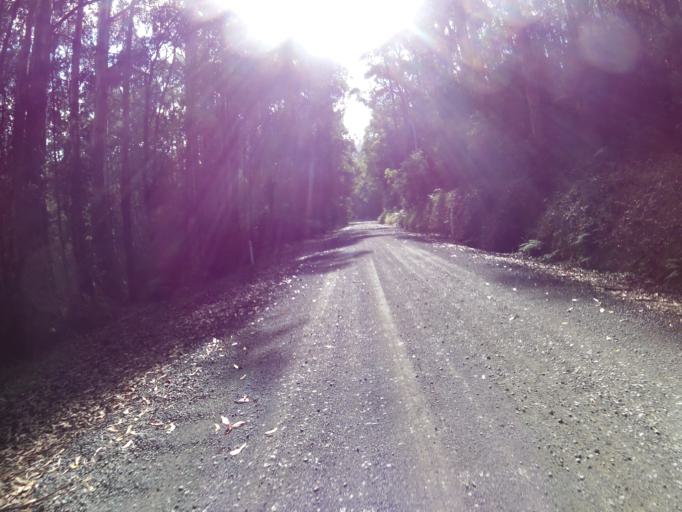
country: AU
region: Victoria
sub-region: Yarra Ranges
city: Millgrove
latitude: -37.8615
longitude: 145.8065
